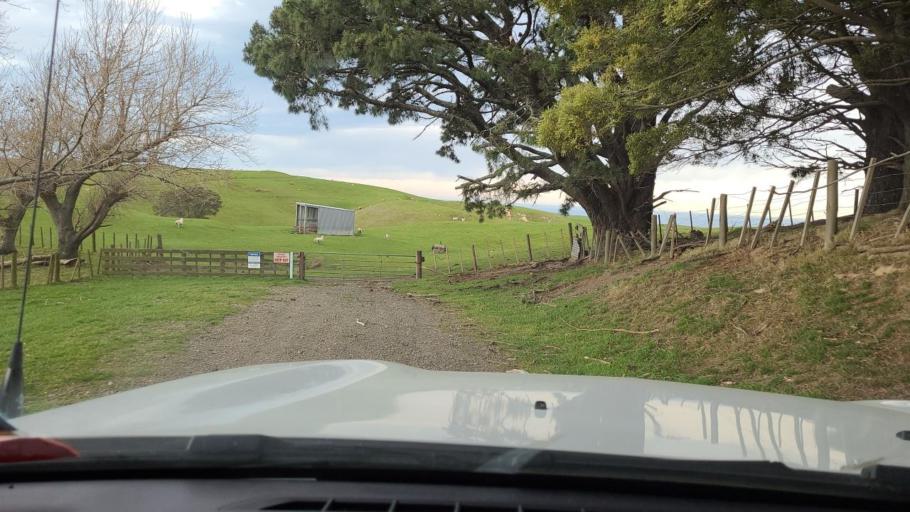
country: NZ
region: Hawke's Bay
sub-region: Napier City
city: Napier
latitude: -39.2259
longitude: 177.0088
